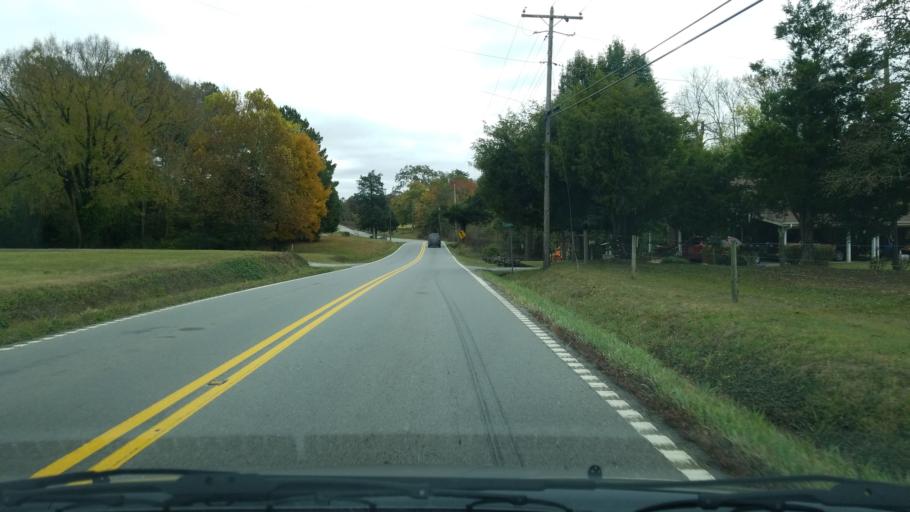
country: US
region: Tennessee
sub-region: Hamilton County
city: Sale Creek
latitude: 35.3749
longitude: -84.9973
